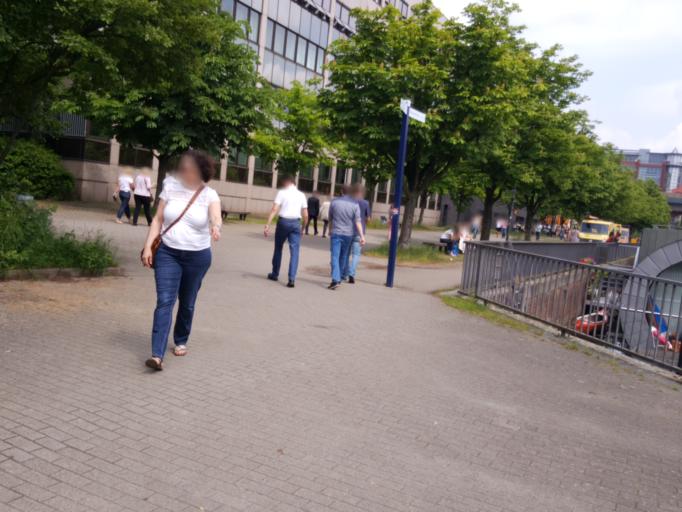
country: DE
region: Hamburg
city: Hamburg-Mitte
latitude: 53.5465
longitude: 10.0202
